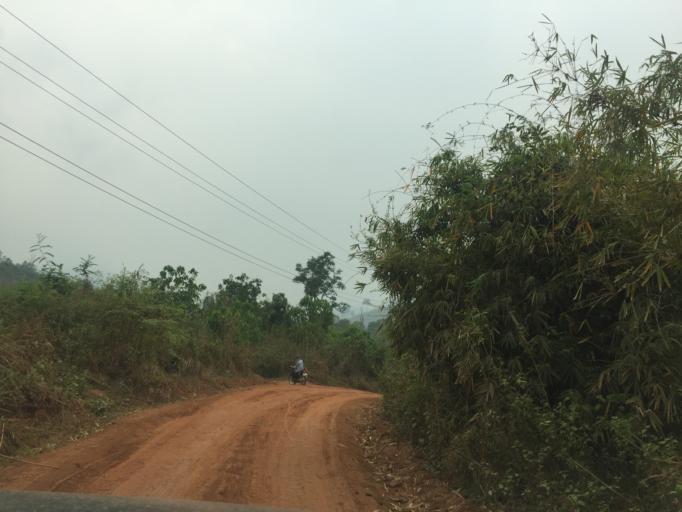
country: TH
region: Nan
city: Bo Kluea
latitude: 18.8543
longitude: 101.4231
